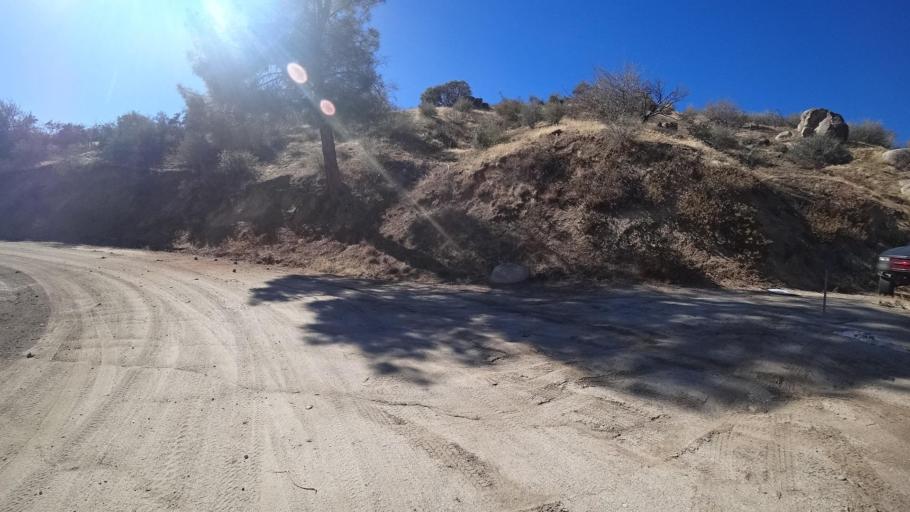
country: US
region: California
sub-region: Kern County
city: Alta Sierra
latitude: 35.7083
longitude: -118.5061
